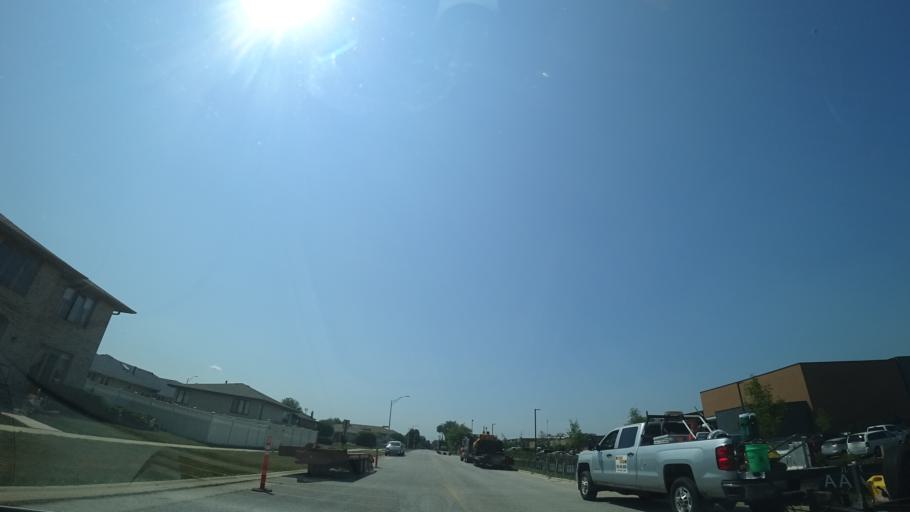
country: US
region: Illinois
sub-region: Cook County
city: Oak Lawn
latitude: 41.6980
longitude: -87.7553
